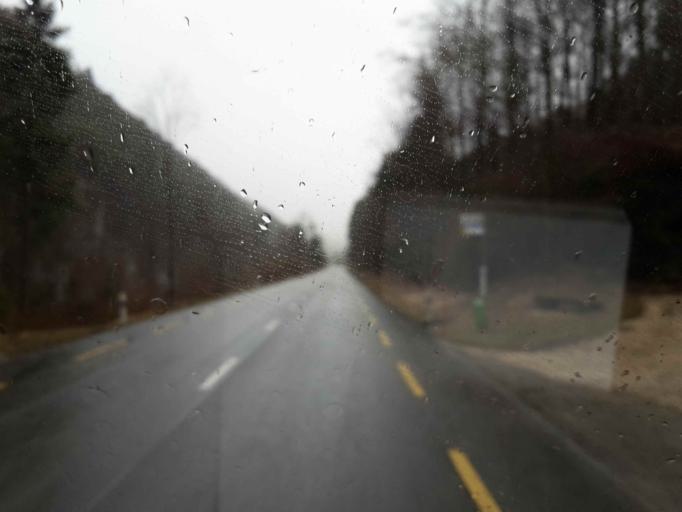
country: CH
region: Solothurn
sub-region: Bezirk Thal
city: Welschenrohr
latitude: 47.2831
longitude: 7.5550
